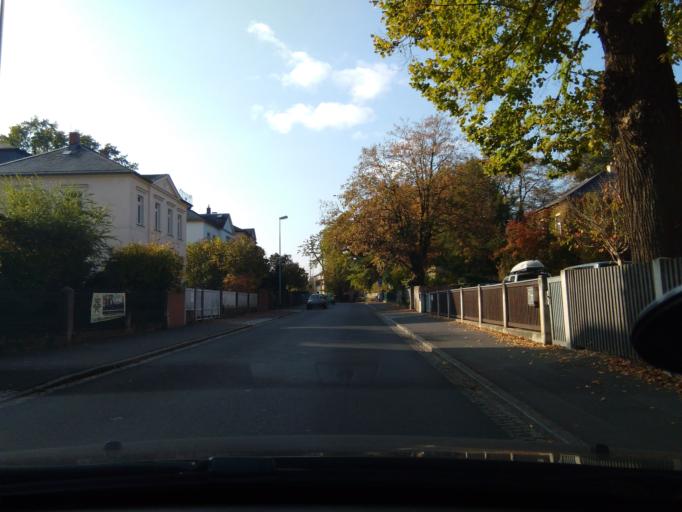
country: DE
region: Saxony
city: Coswig
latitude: 51.1209
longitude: 13.5748
